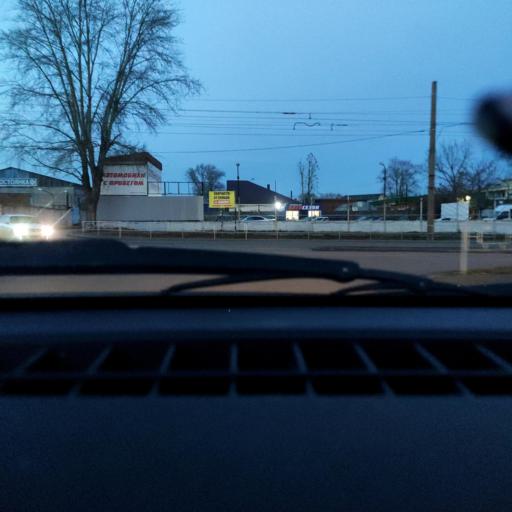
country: RU
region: Bashkortostan
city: Ufa
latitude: 54.8233
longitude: 56.1005
